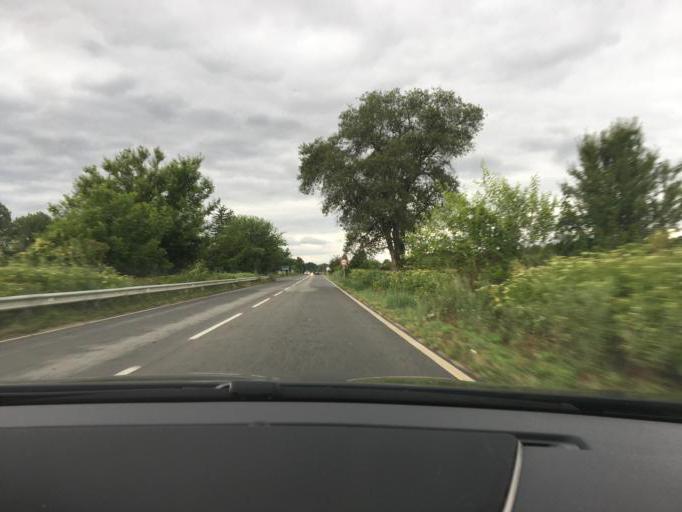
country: BG
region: Kyustendil
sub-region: Obshtina Kyustendil
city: Kyustendil
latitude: 42.2576
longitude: 22.8627
